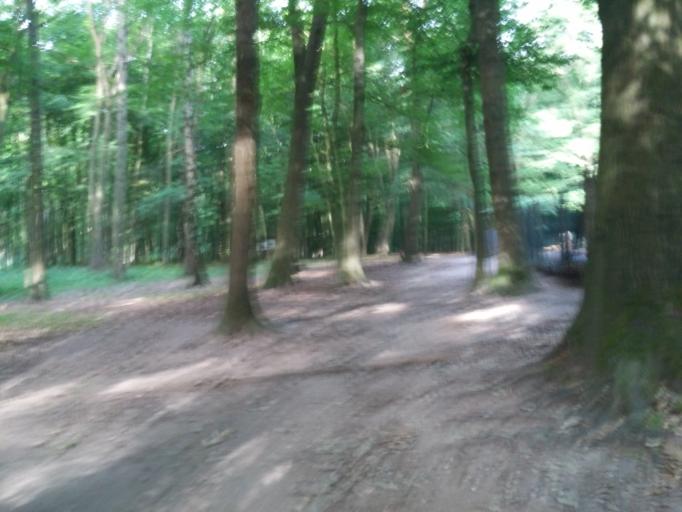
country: DE
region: North Rhine-Westphalia
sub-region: Regierungsbezirk Dusseldorf
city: Krefeld
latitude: 51.3846
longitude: 6.5385
